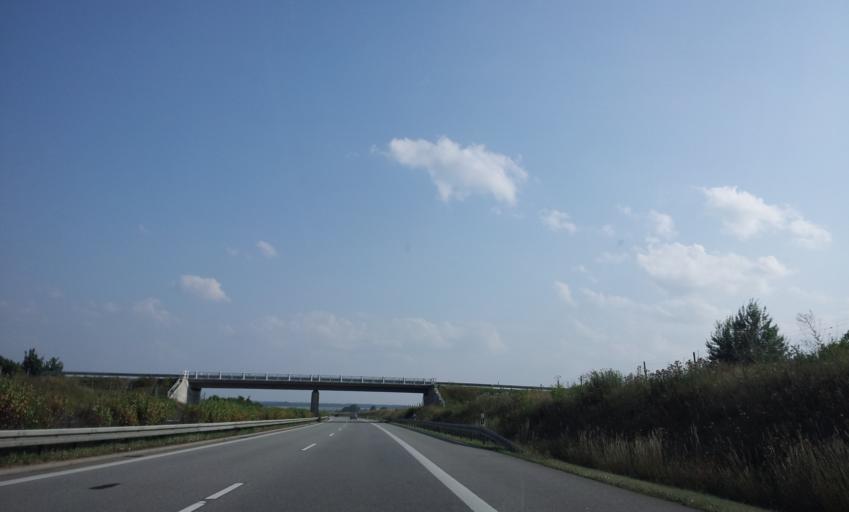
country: DE
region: Mecklenburg-Vorpommern
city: Kessin
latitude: 53.6975
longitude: 13.3255
